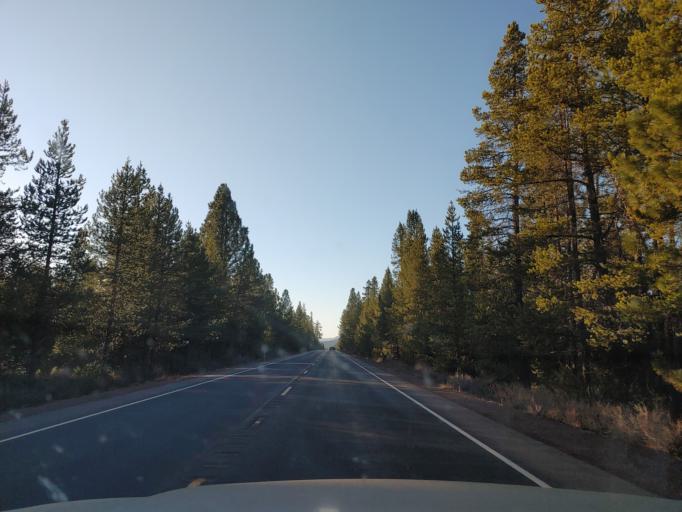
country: US
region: Oregon
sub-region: Deschutes County
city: La Pine
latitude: 43.3896
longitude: -121.8103
